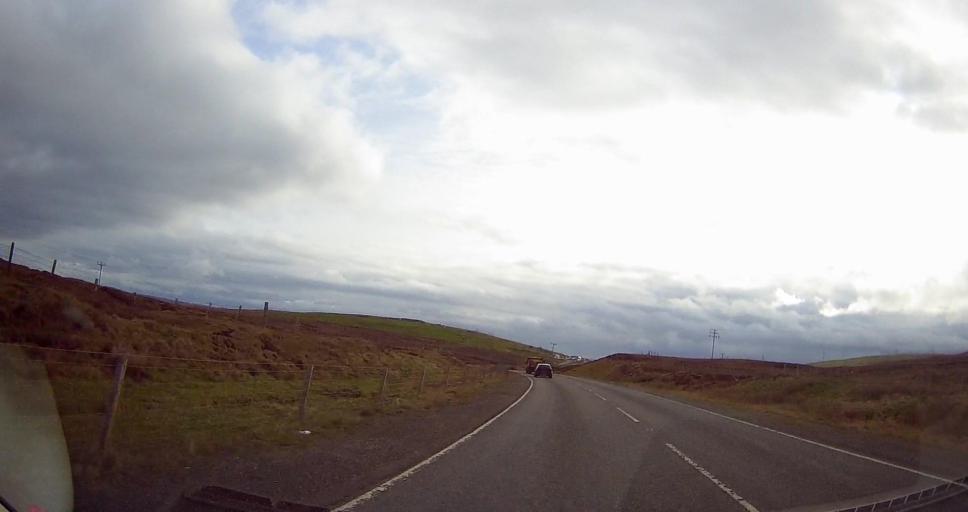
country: GB
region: Scotland
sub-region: Shetland Islands
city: Lerwick
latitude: 60.4415
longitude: -1.2208
